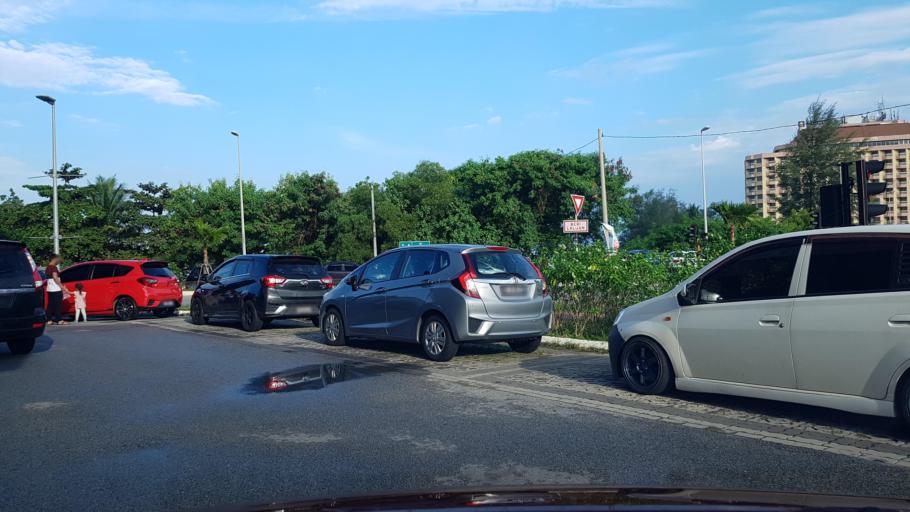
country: MY
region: Terengganu
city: Kuala Terengganu
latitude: 5.3325
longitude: 103.1499
